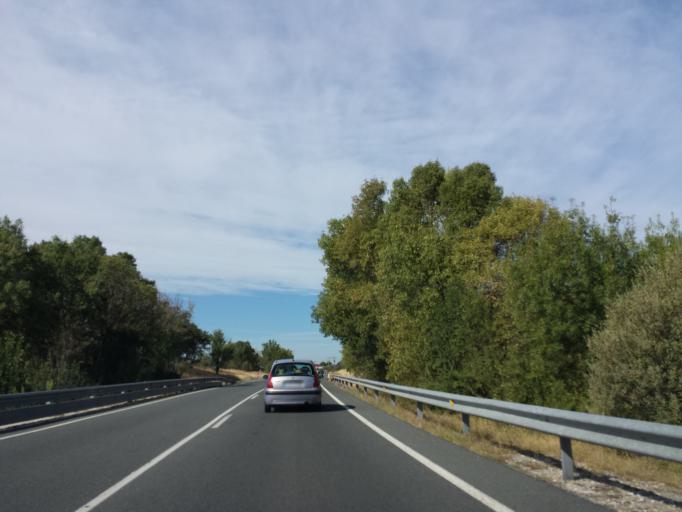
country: ES
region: Castille and Leon
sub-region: Provincia de Avila
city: Casavieja
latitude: 40.2749
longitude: -4.7420
